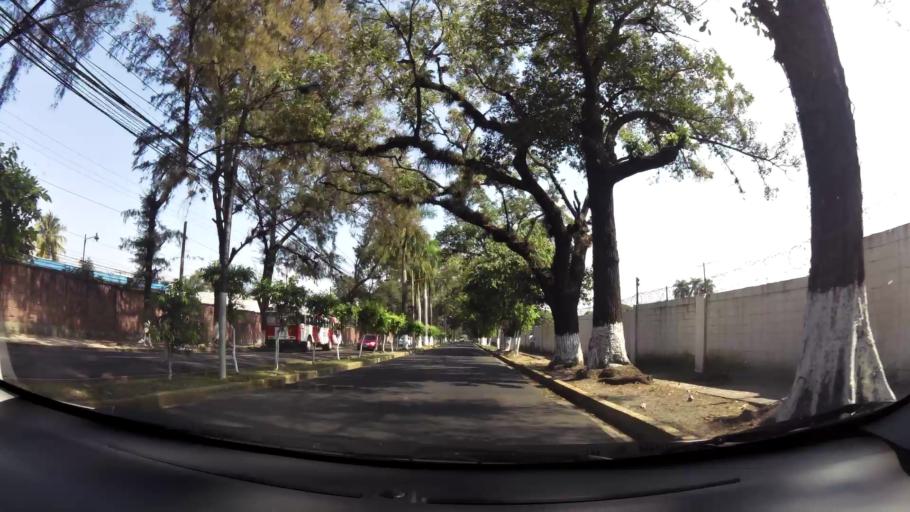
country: SV
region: La Libertad
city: Antiguo Cuscatlan
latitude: 13.6870
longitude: -89.2360
